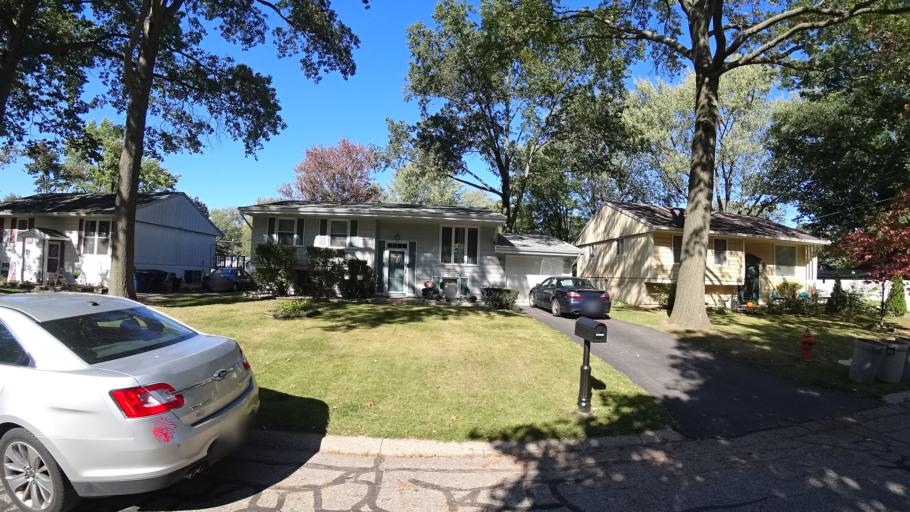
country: US
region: Indiana
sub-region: LaPorte County
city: Michigan City
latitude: 41.6912
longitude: -86.8997
